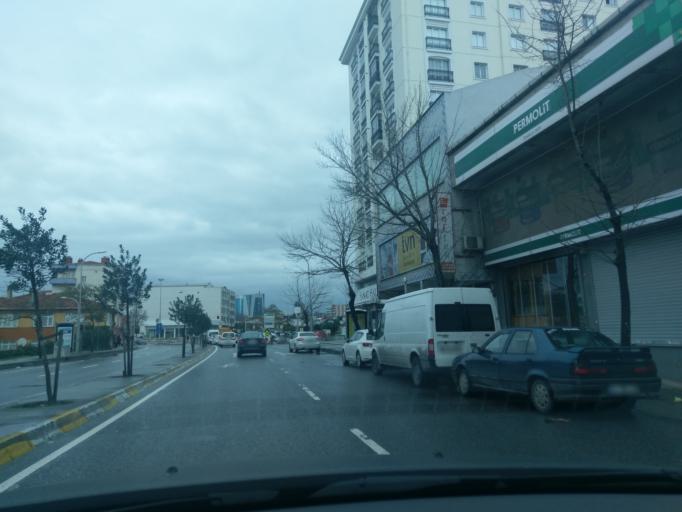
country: TR
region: Istanbul
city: Mahmutbey
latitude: 41.0518
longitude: 28.8302
